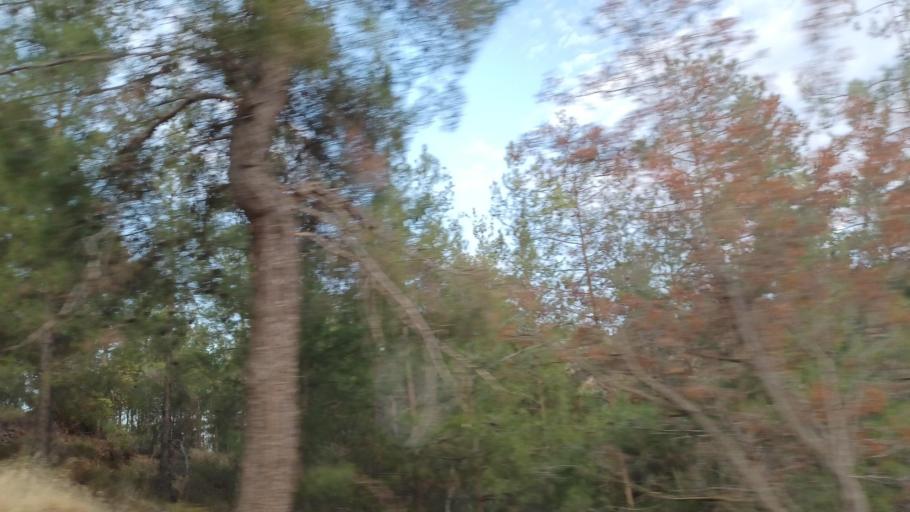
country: CY
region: Limassol
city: Kyperounta
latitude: 34.9362
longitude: 32.9327
